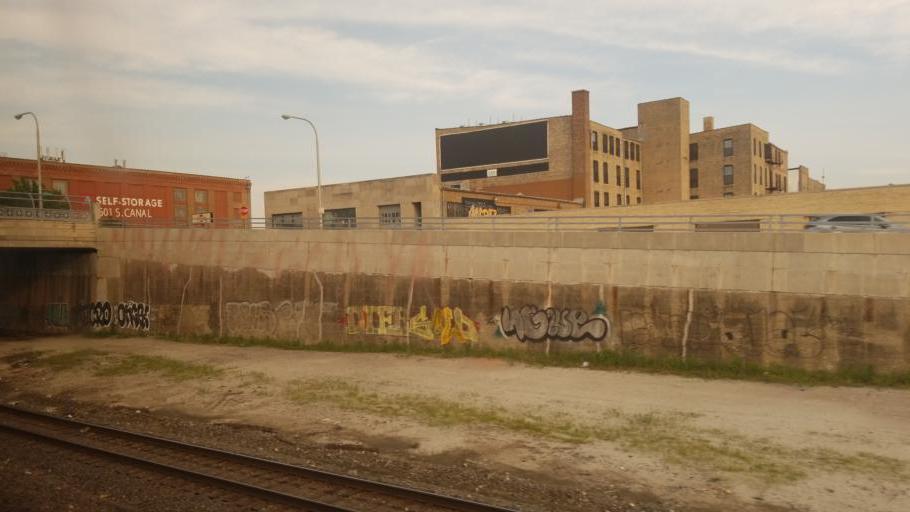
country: US
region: Illinois
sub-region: Cook County
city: Chicago
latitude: 41.8602
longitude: -87.6398
